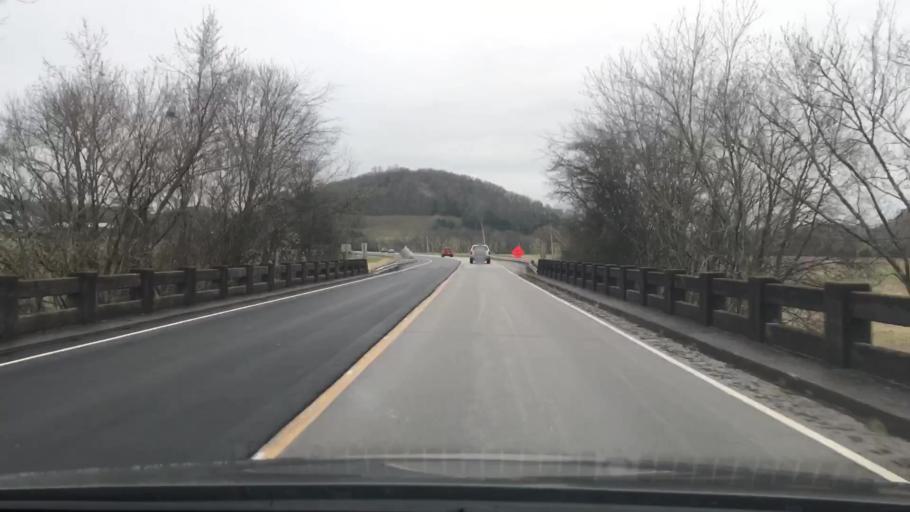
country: US
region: Tennessee
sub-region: Smith County
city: Carthage
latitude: 36.3086
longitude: -86.0078
